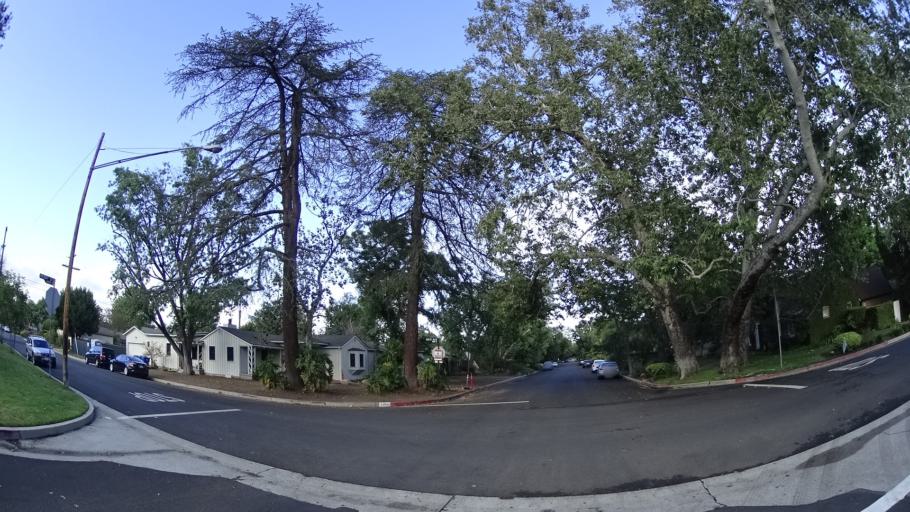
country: US
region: California
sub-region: Los Angeles County
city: North Hollywood
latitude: 34.1622
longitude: -118.3946
